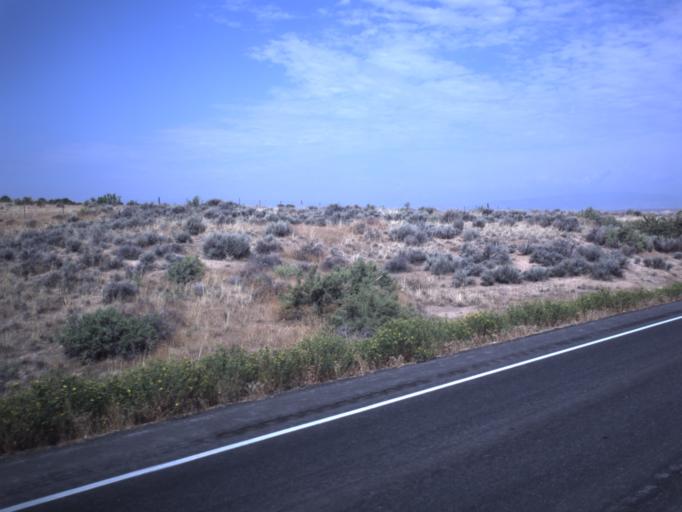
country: US
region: Utah
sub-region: Uintah County
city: Naples
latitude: 40.3551
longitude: -109.3118
